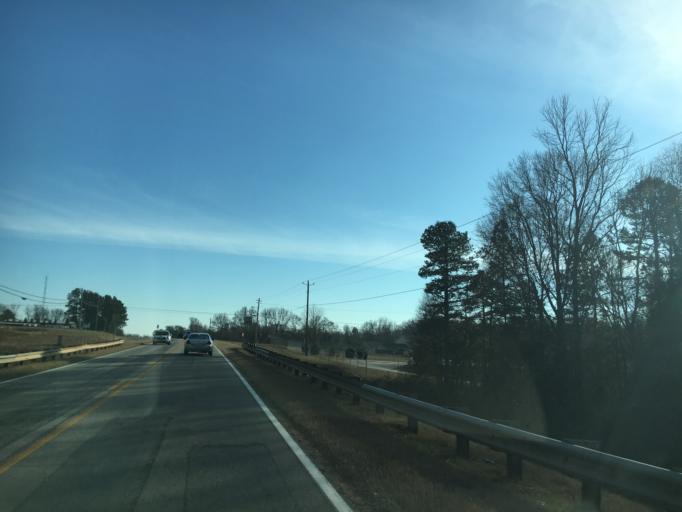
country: US
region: Georgia
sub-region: Hart County
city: Hartwell
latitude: 34.3702
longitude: -82.9388
